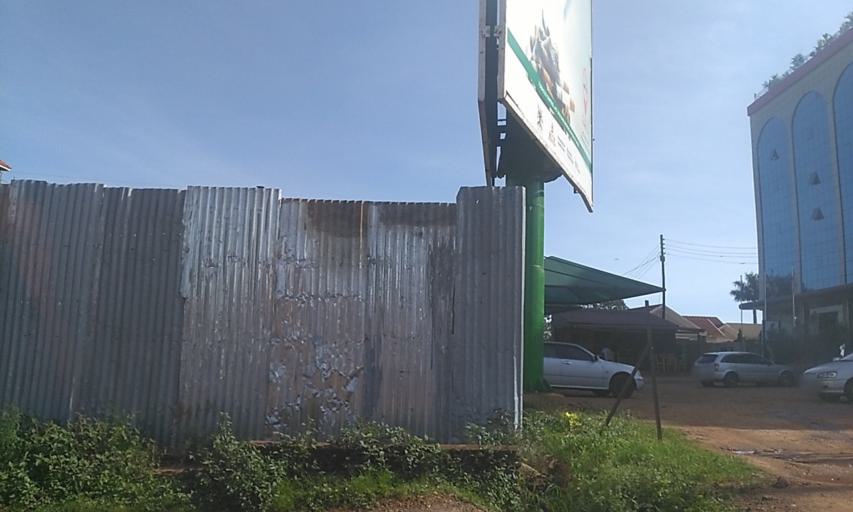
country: UG
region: Central Region
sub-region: Wakiso District
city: Kireka
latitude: 0.3619
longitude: 32.6215
